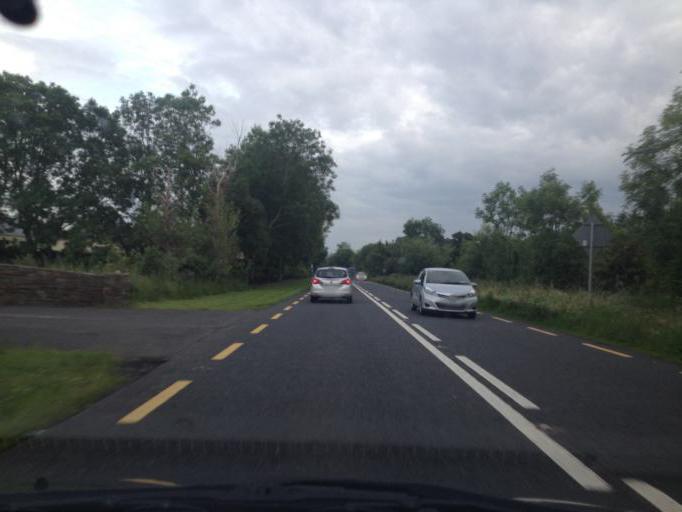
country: IE
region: Connaught
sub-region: Sligo
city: Sligo
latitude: 54.3460
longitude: -8.5039
